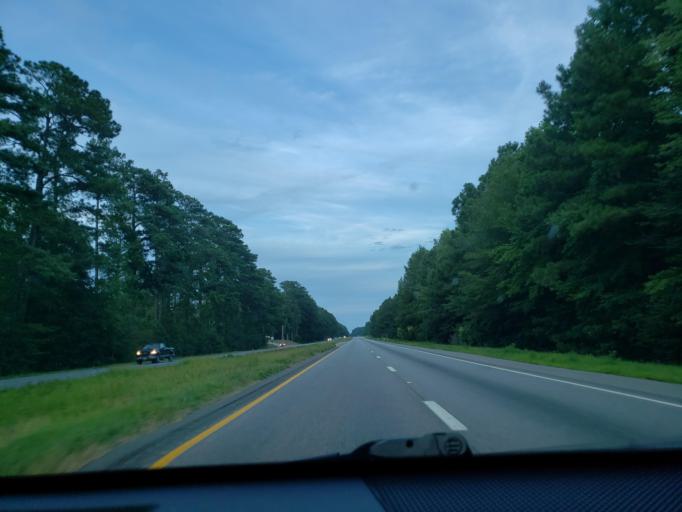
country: US
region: Virginia
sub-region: Sussex County
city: Sussex
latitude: 36.7060
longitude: -77.2922
